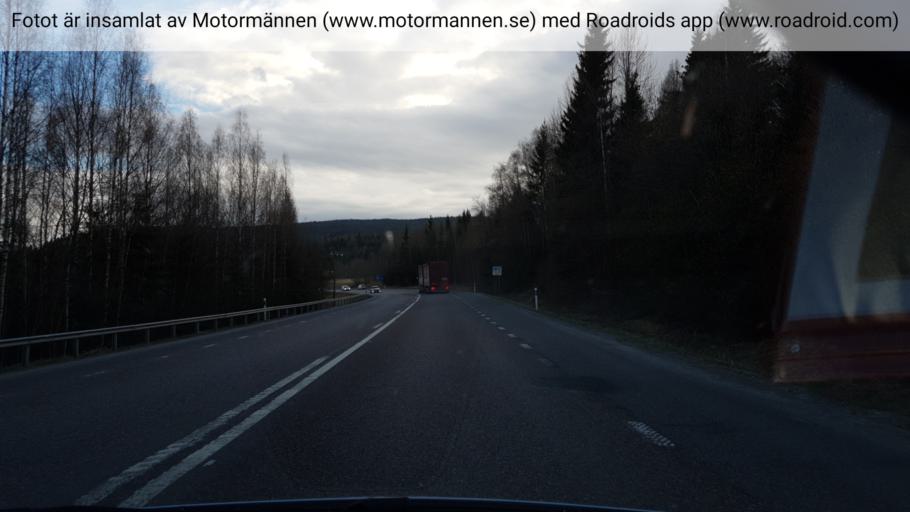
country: SE
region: Vaesternorrland
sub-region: Kramfors Kommun
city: Kramfors
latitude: 62.8851
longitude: 17.8511
